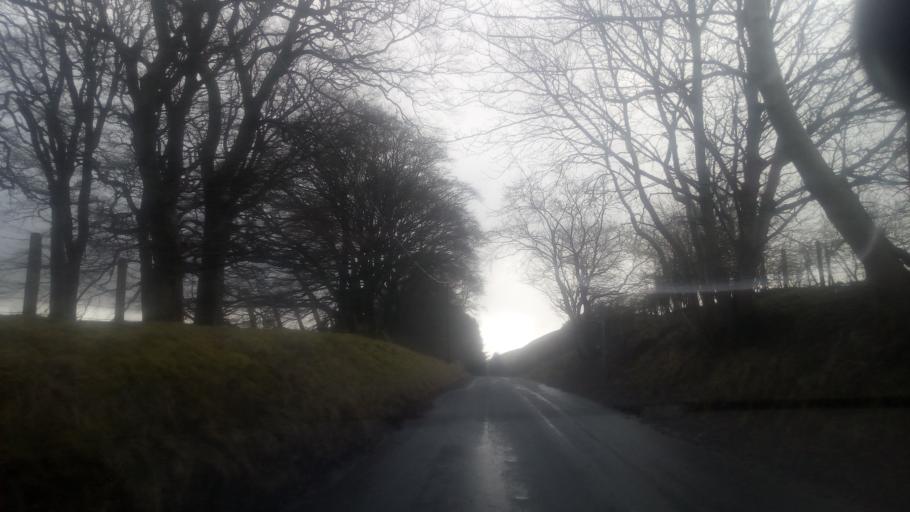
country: GB
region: Scotland
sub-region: The Scottish Borders
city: Innerleithen
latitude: 55.4546
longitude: -3.1002
